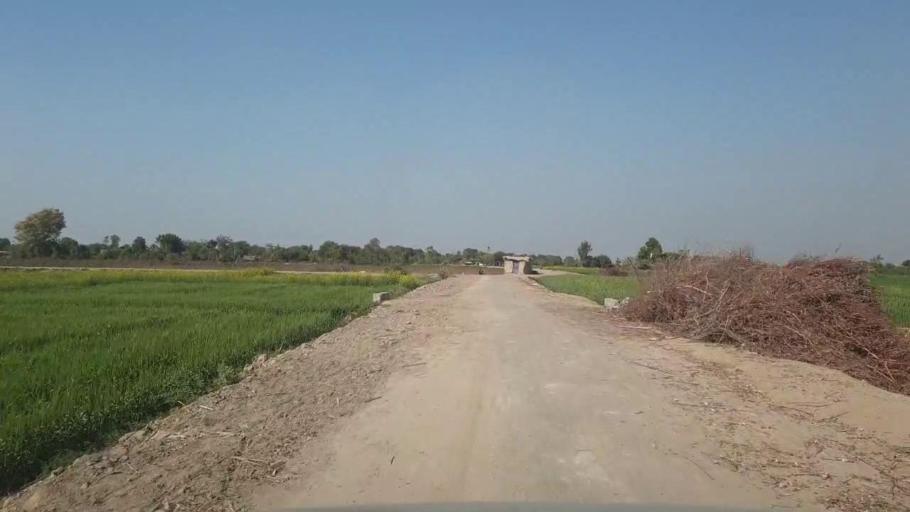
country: PK
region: Sindh
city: Chambar
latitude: 25.3238
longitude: 68.8526
